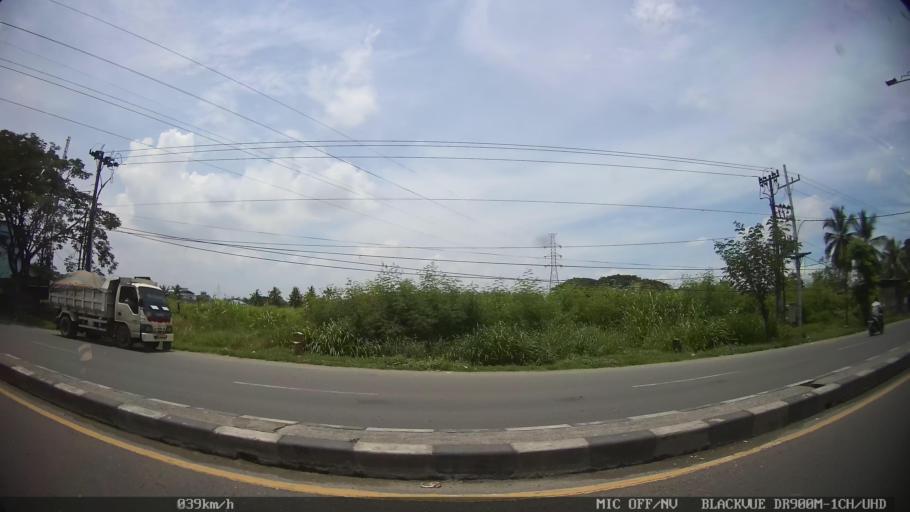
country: ID
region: North Sumatra
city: Labuhan Deli
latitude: 3.7259
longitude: 98.6782
